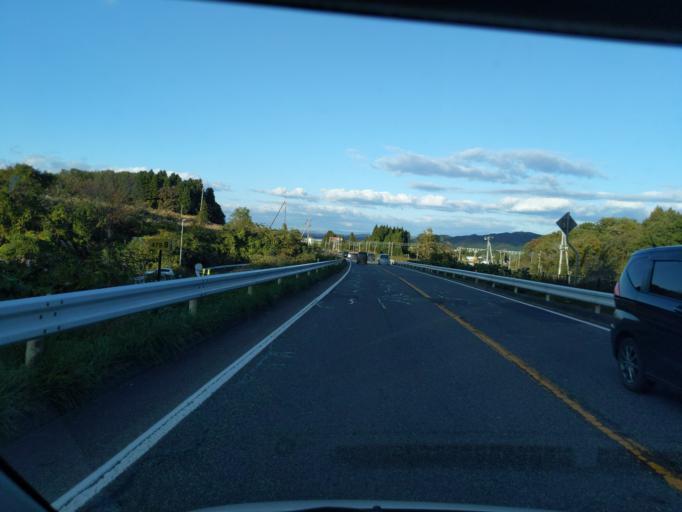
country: JP
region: Iwate
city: Kitakami
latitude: 39.2383
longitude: 141.0967
